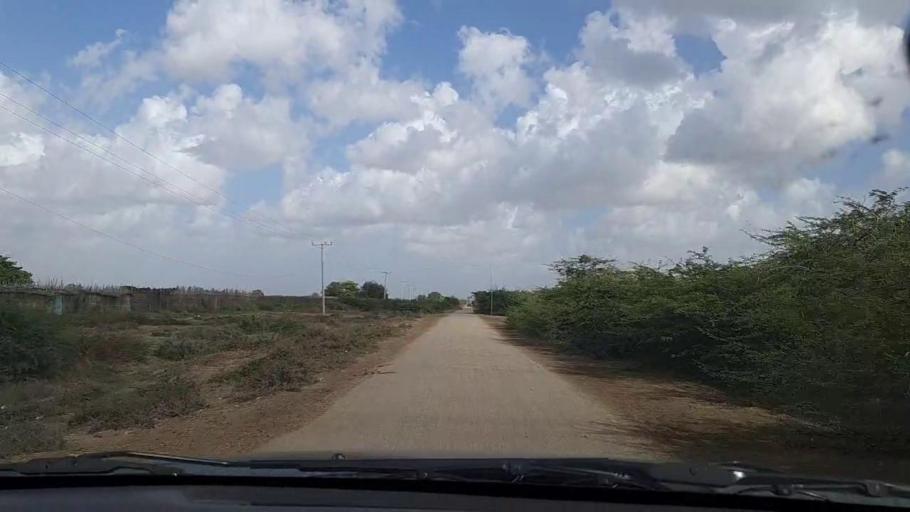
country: PK
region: Sindh
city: Keti Bandar
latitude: 24.0988
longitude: 67.6017
